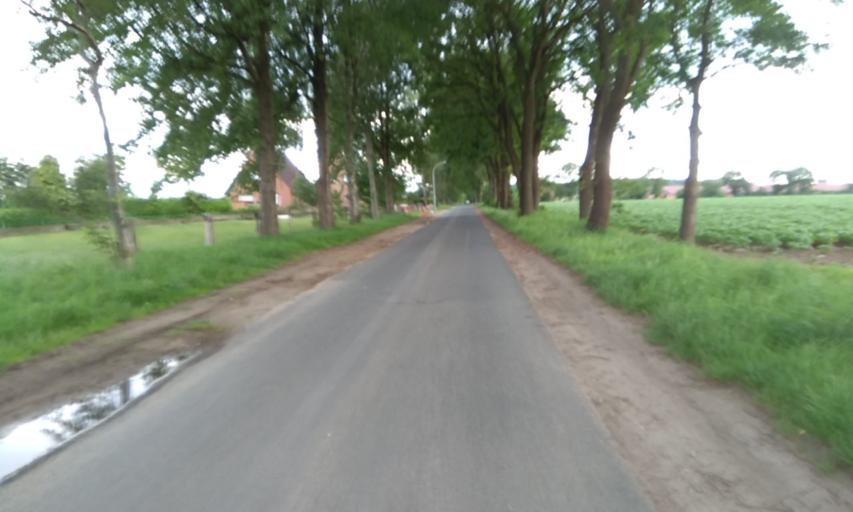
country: DE
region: Lower Saxony
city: Regesbostel
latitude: 53.3826
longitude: 9.6412
